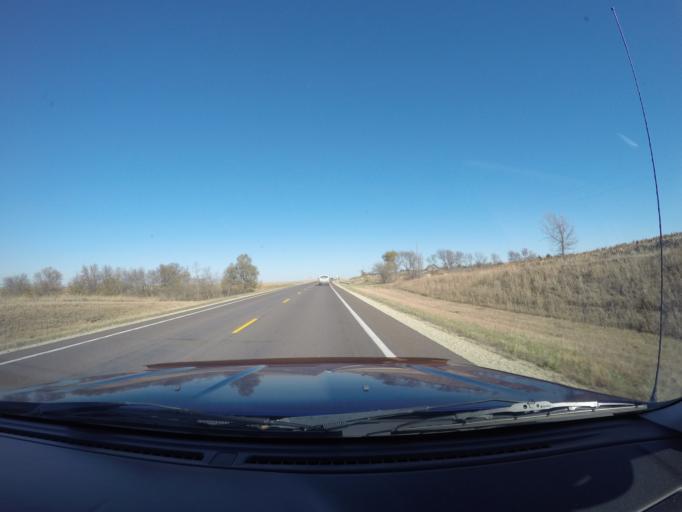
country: US
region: Kansas
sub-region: Marshall County
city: Blue Rapids
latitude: 39.5218
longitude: -96.7553
